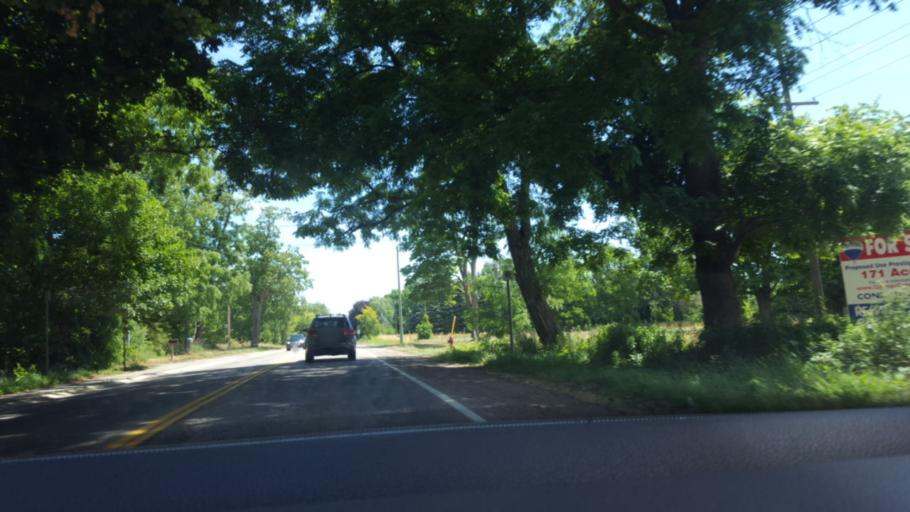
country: CA
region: Ontario
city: Ancaster
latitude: 43.2035
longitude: -79.9716
